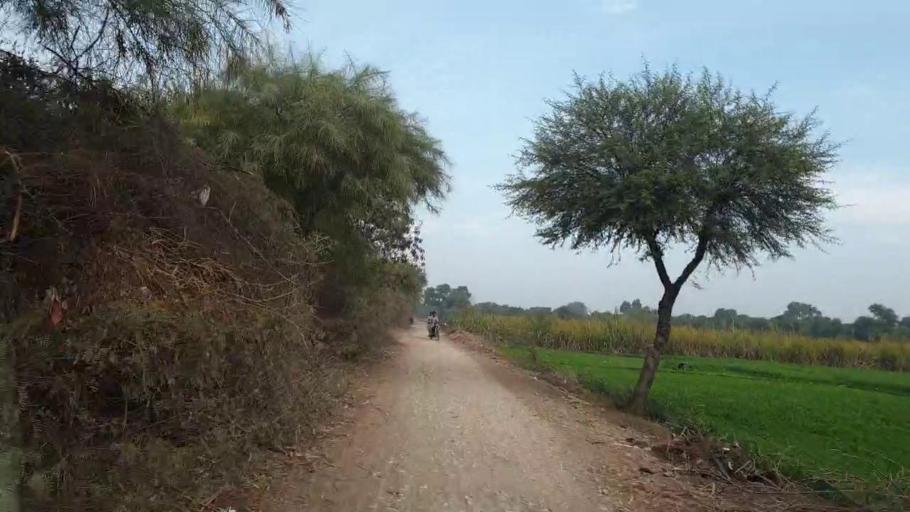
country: PK
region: Sindh
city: Matiari
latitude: 25.5568
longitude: 68.5300
